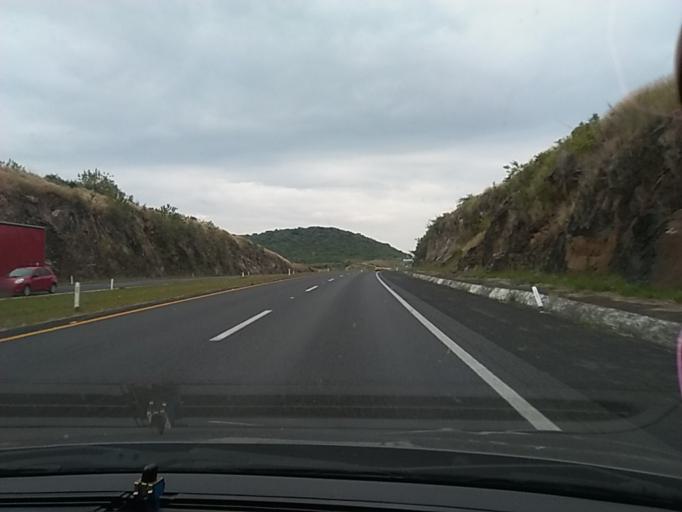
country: MX
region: Michoacan
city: Penjamillo de Degollado
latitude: 20.0442
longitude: -101.9400
